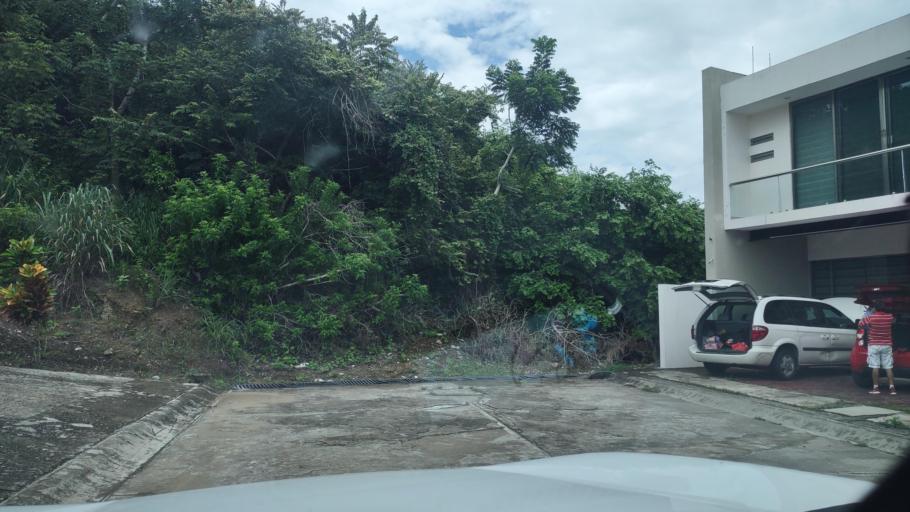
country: MX
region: Veracruz
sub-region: Tuxpan
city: Alto Lucero
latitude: 20.9437
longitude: -97.4274
